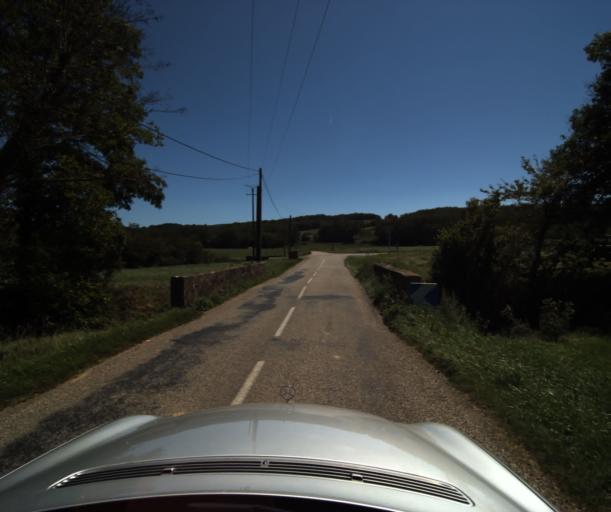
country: FR
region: Midi-Pyrenees
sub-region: Departement de l'Ariege
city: Belesta
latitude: 42.9816
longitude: 1.9166
